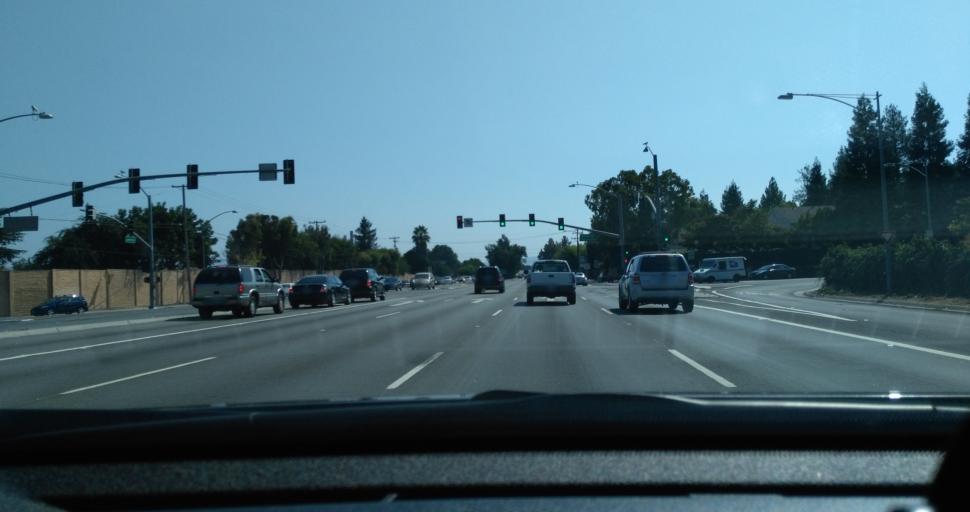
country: US
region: California
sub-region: Santa Clara County
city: Sunnyvale
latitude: 37.3604
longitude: -121.9961
